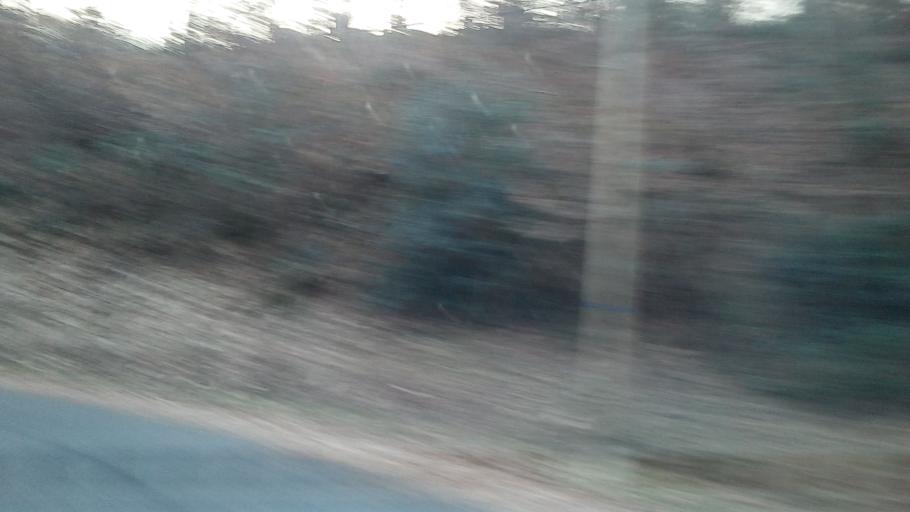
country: FR
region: Limousin
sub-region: Departement de la Correze
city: Naves
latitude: 45.3015
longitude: 1.7832
